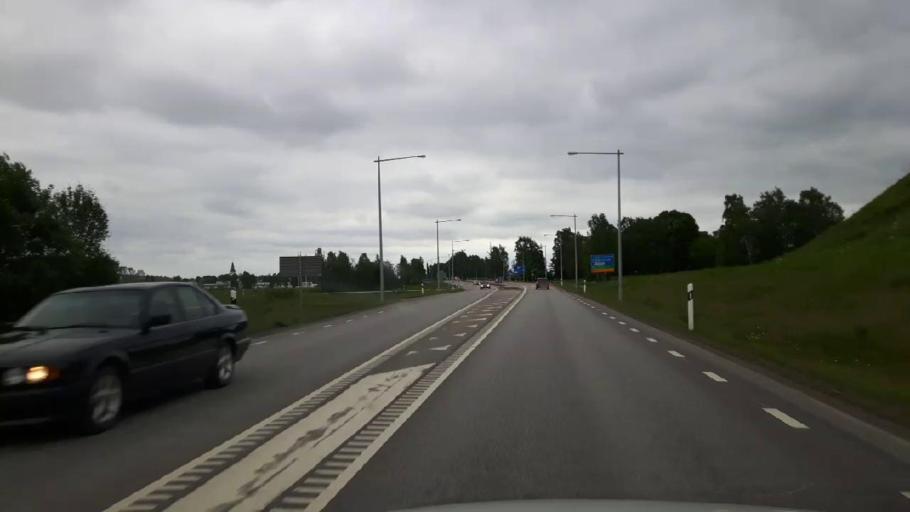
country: SE
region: Vaestmanland
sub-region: Kopings Kommun
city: Koping
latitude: 59.5233
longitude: 15.9651
